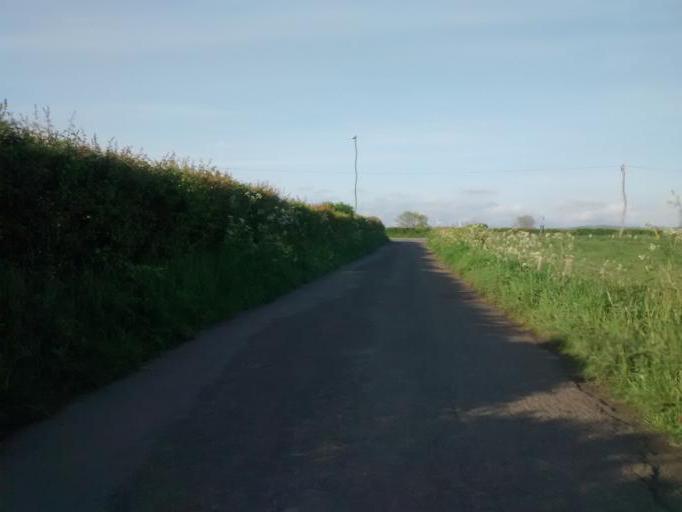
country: GB
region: England
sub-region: County Durham
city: Coxhoe
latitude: 54.7461
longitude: -1.5350
